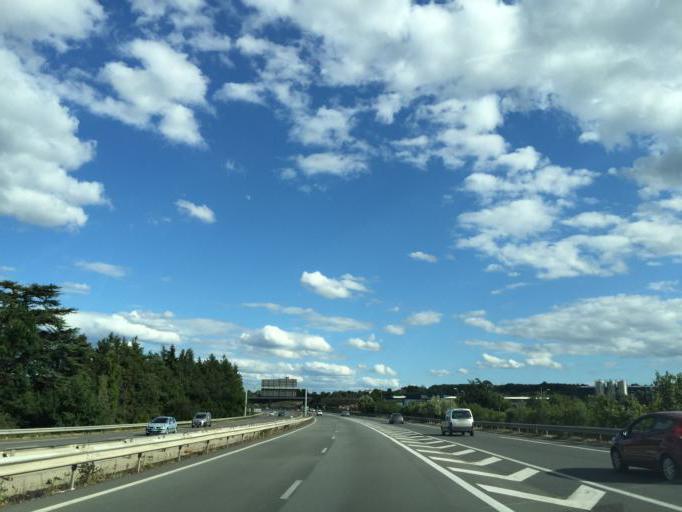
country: FR
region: Rhone-Alpes
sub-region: Departement de la Loire
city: Andrezieux-Boutheon
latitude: 45.5257
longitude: 4.2878
